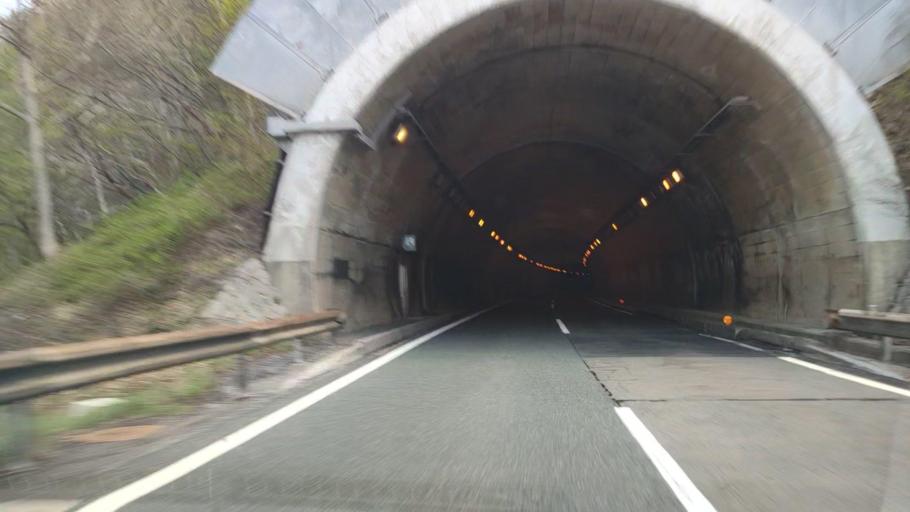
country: JP
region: Akita
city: Hanawa
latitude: 40.0758
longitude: 141.0236
